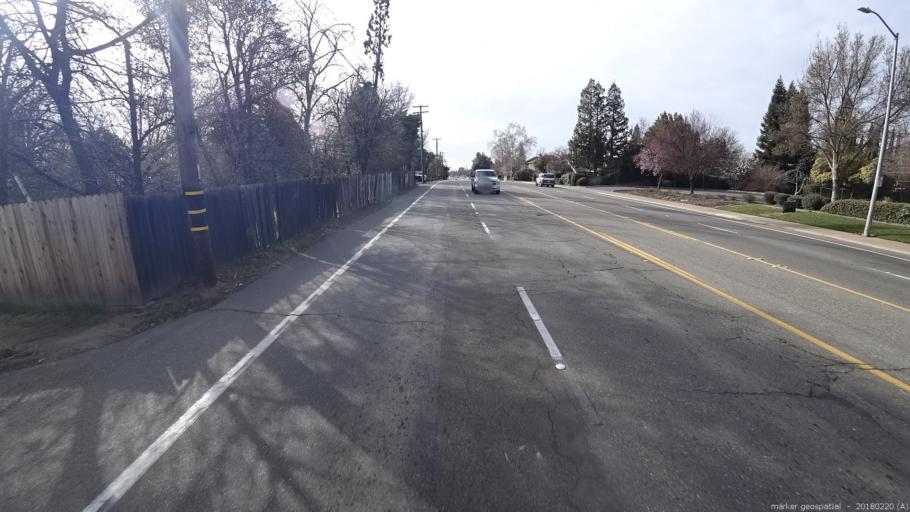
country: US
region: California
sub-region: Sacramento County
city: Orangevale
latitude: 38.6835
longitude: -121.2255
